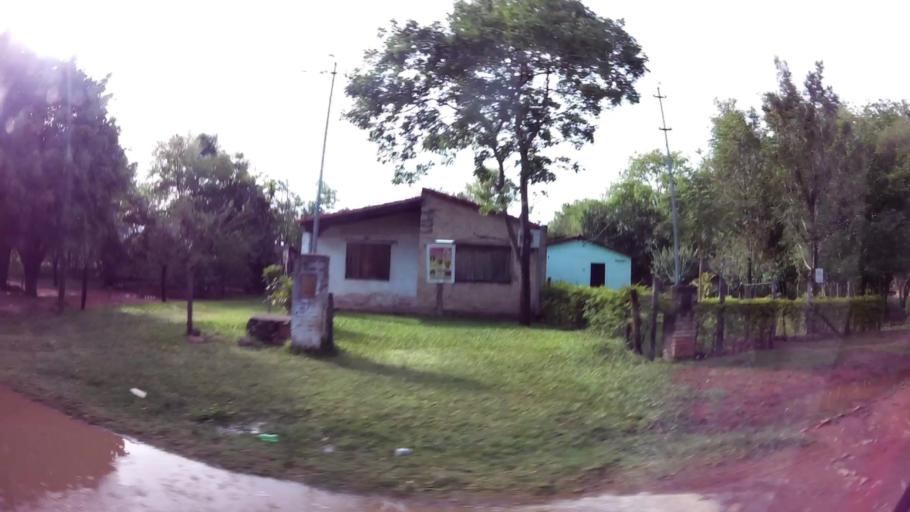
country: PY
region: Central
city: Limpio
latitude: -25.1880
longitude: -57.4835
